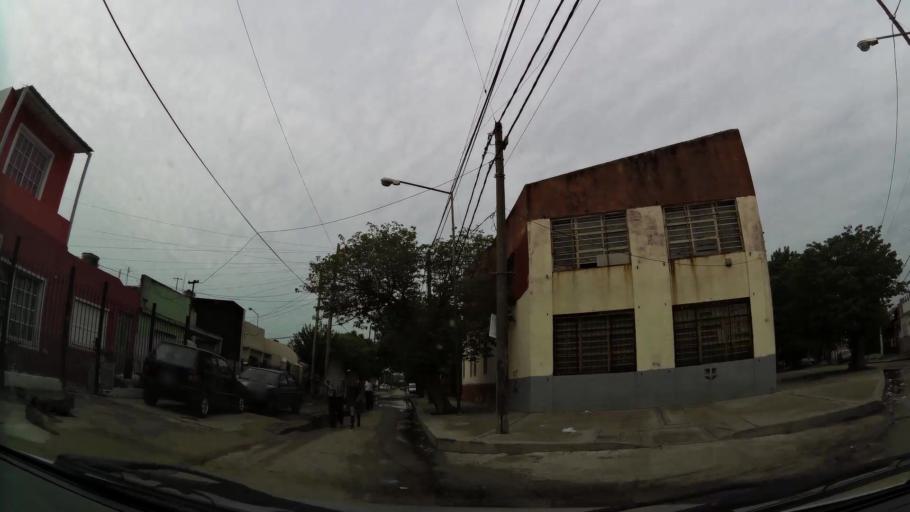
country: AR
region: Buenos Aires
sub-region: Partido de Lanus
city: Lanus
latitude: -34.7240
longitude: -58.3419
